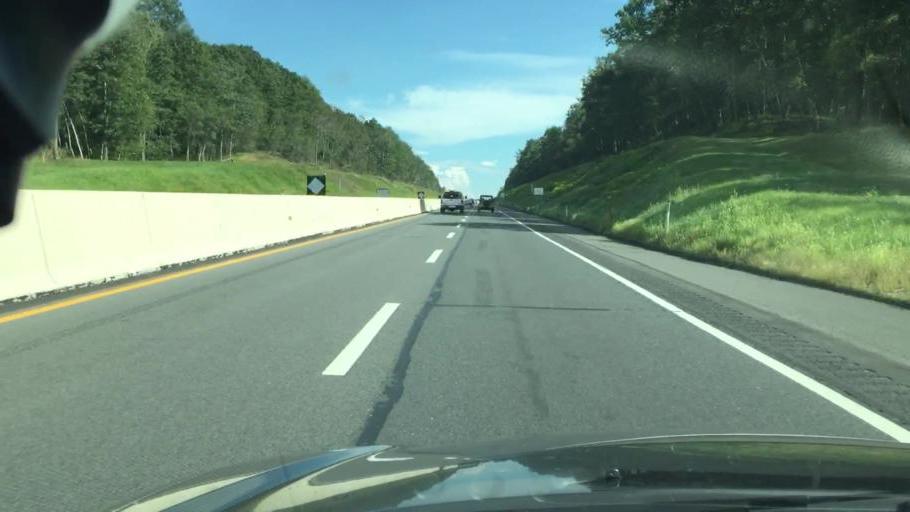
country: US
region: Pennsylvania
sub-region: Luzerne County
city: White Haven
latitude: 41.0661
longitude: -75.6915
